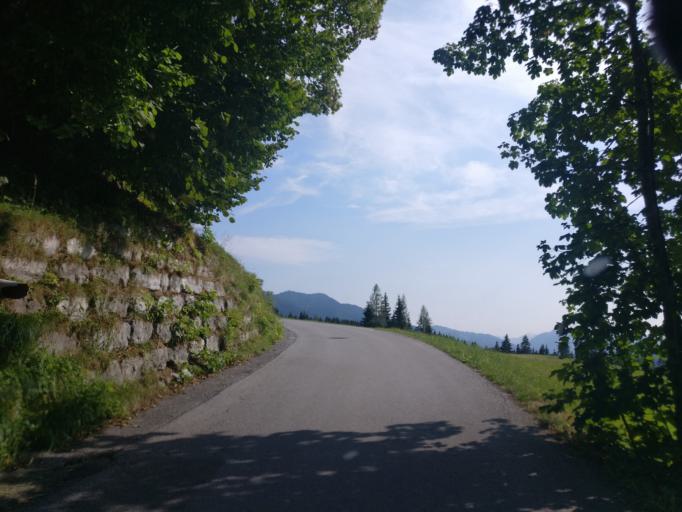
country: AT
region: Salzburg
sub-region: Politischer Bezirk Sankt Johann im Pongau
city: Werfenweng
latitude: 47.4634
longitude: 13.2410
